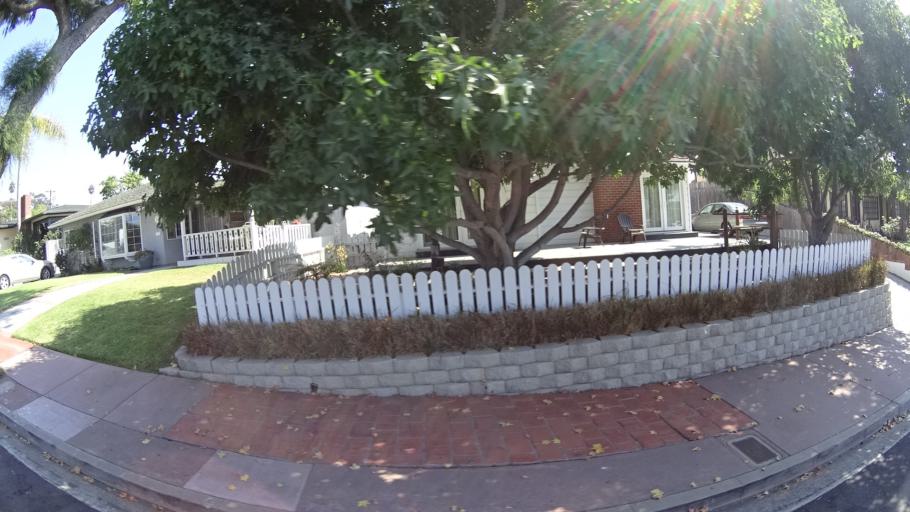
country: US
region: California
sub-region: Orange County
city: San Clemente
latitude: 33.4216
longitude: -117.6107
